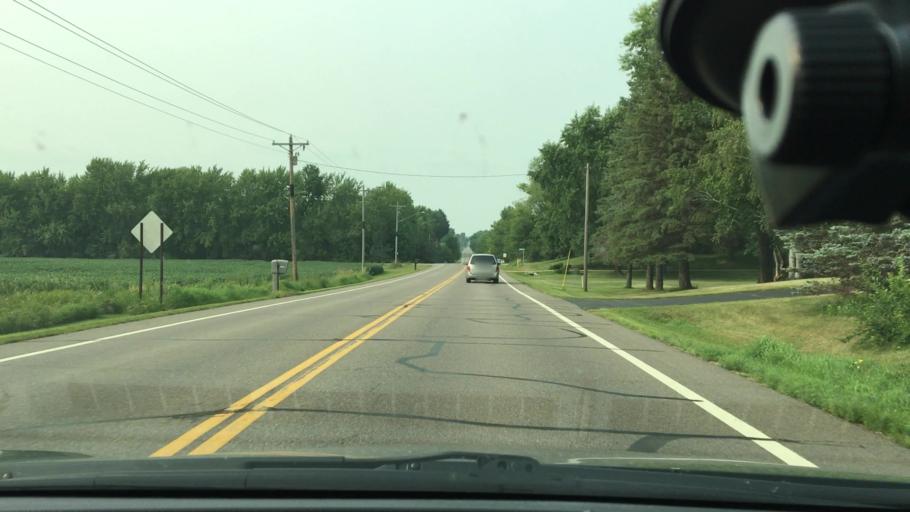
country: US
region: Minnesota
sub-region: Hennepin County
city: Champlin
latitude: 45.1654
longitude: -93.4621
